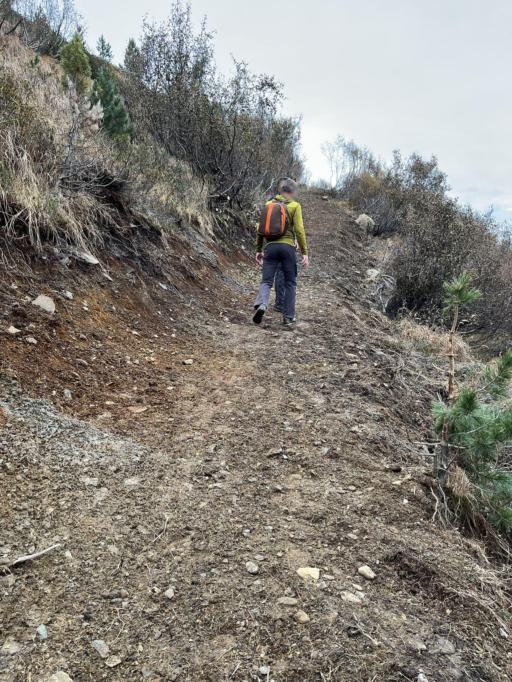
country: IT
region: Lombardy
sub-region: Provincia di Sondrio
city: Sant'Antonio
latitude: 46.4107
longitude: 10.5343
